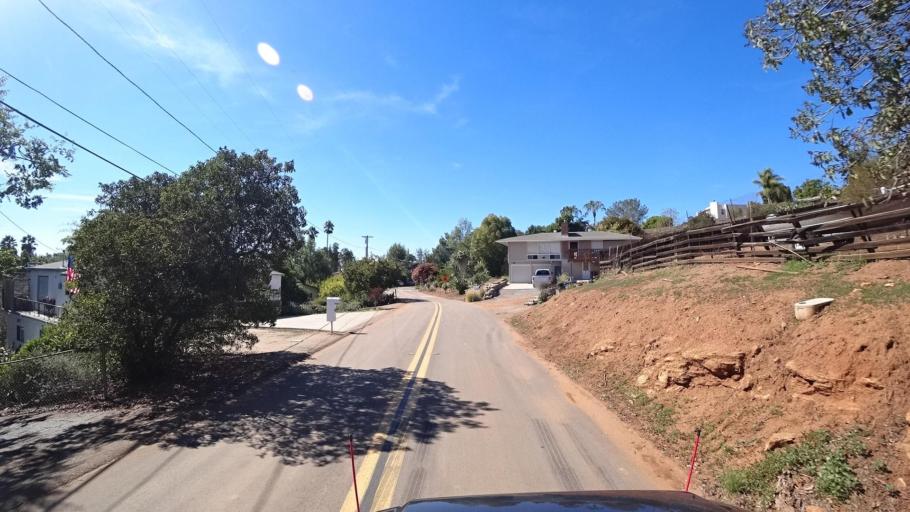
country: US
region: California
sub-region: San Diego County
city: Casa de Oro-Mount Helix
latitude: 32.7572
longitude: -116.9643
